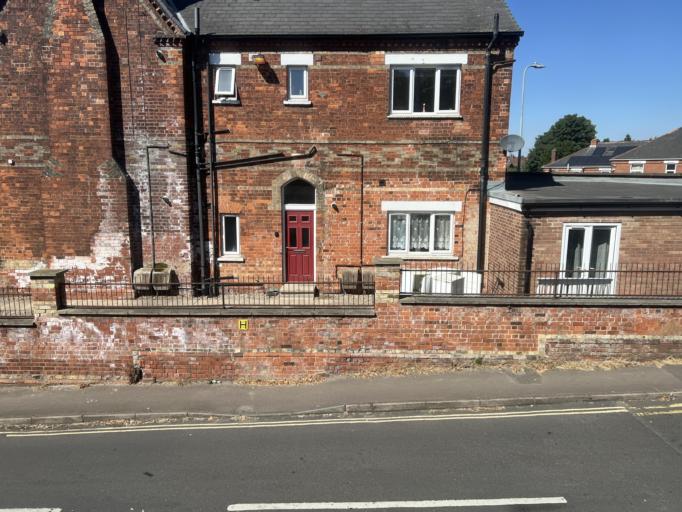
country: GB
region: England
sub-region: Lincolnshire
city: Boston
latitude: 52.9812
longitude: -0.0302
